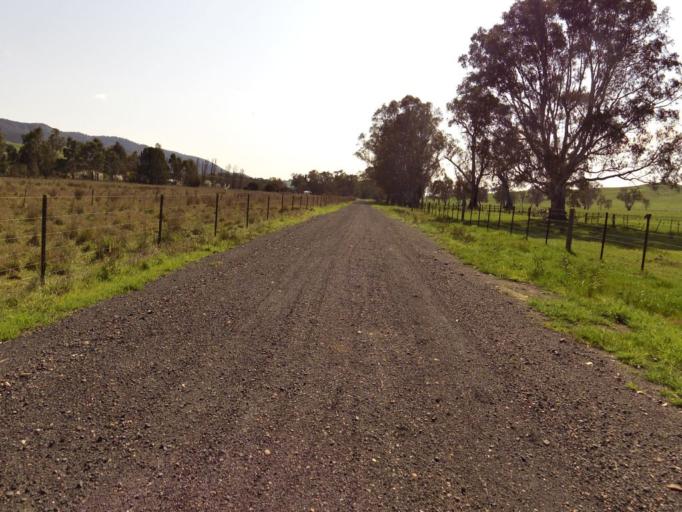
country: AU
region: Victoria
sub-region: Murrindindi
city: Alexandra
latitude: -37.1466
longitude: 145.5879
